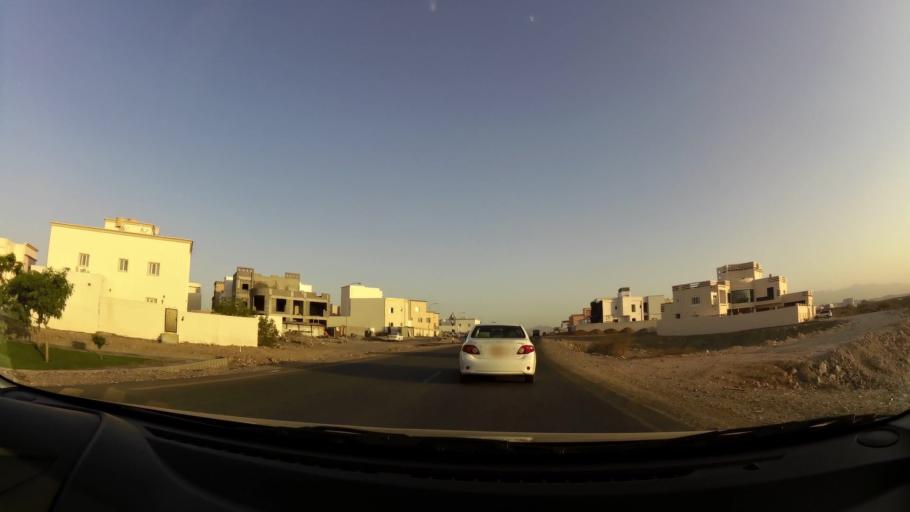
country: OM
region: Muhafazat Masqat
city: As Sib al Jadidah
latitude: 23.6100
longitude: 58.1935
